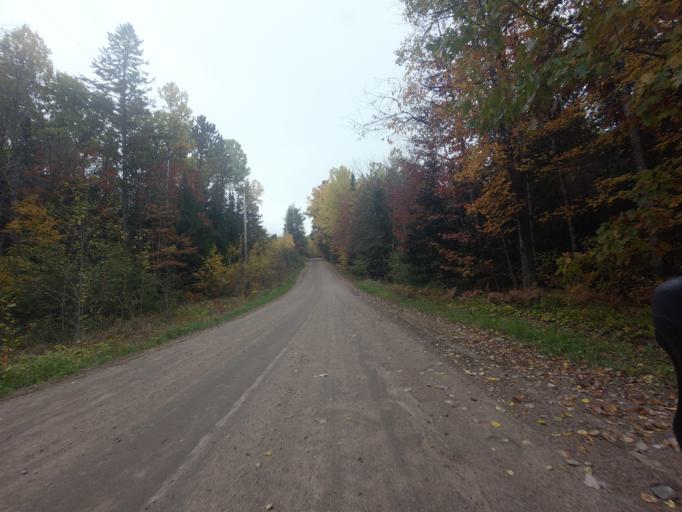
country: CA
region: Ontario
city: Pembroke
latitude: 45.7378
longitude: -77.2239
